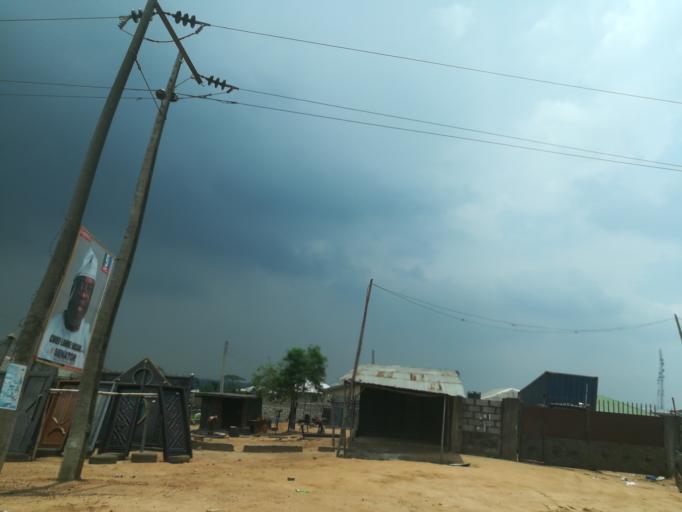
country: NG
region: Lagos
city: Ikorodu
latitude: 6.6073
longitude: 3.5854
